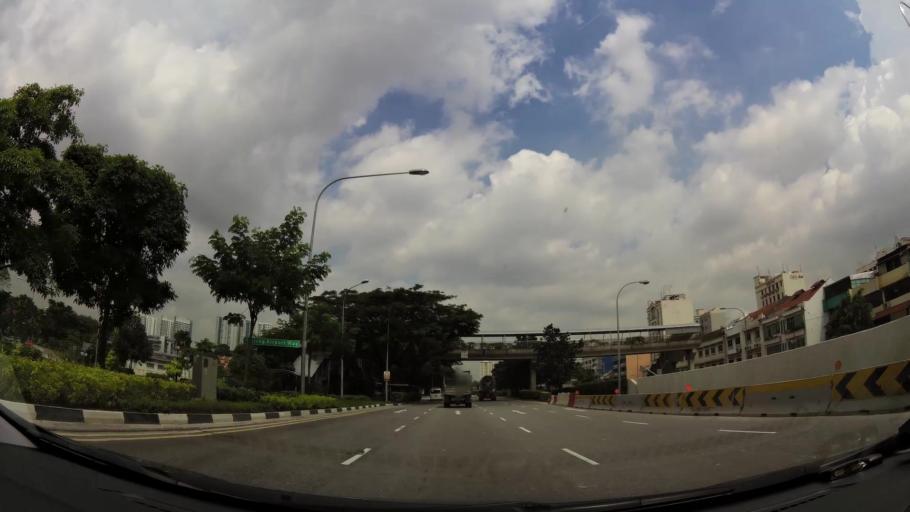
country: SG
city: Singapore
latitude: 1.3090
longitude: 103.8758
